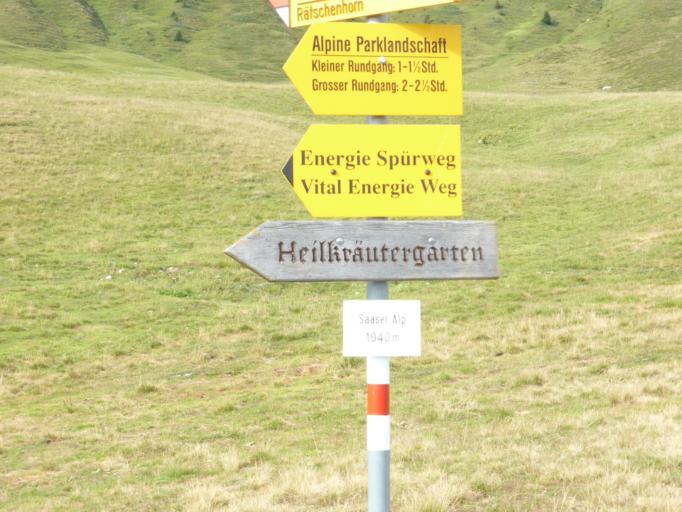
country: CH
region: Grisons
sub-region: Praettigau/Davos District
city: Klosters Serneus
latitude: 46.9055
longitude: 9.8618
